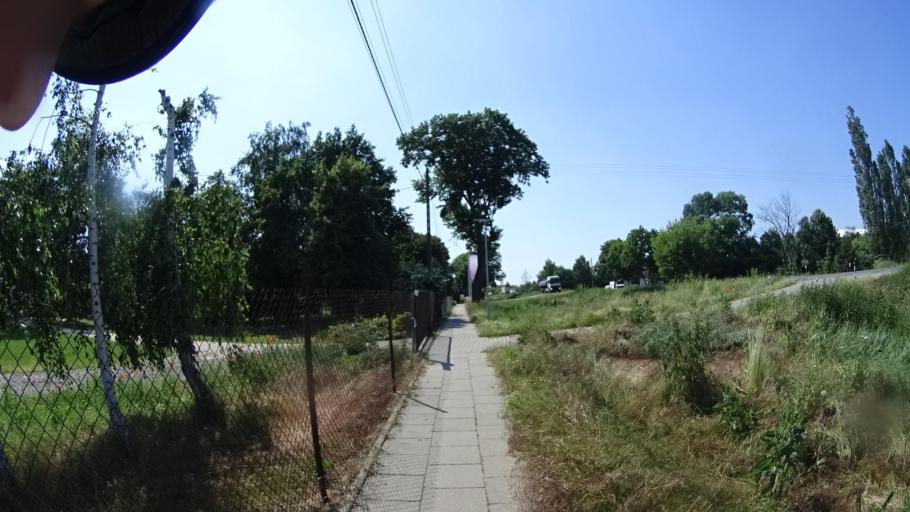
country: PL
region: Masovian Voivodeship
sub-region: Powiat warszawski zachodni
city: Bieniewice
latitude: 52.1999
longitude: 20.5803
